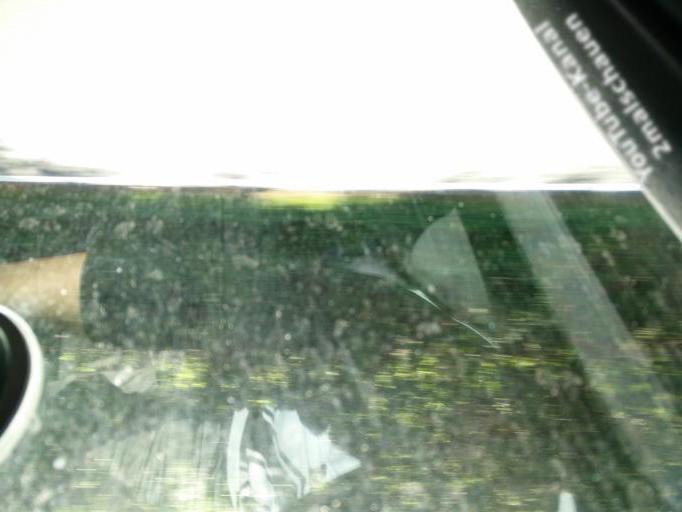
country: DE
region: Saxony
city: Waldheim
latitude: 51.0617
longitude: 13.0214
